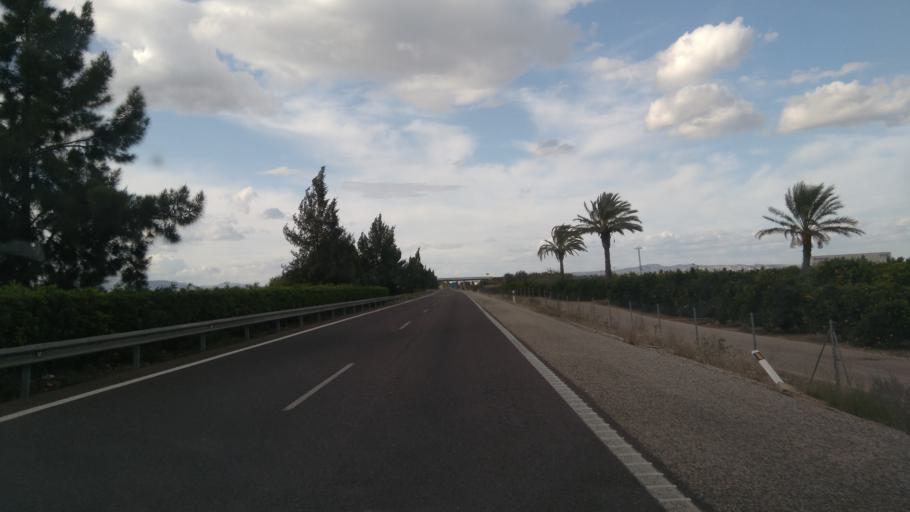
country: ES
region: Valencia
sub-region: Provincia de Valencia
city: Guadassuar
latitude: 39.1671
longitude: -0.4607
